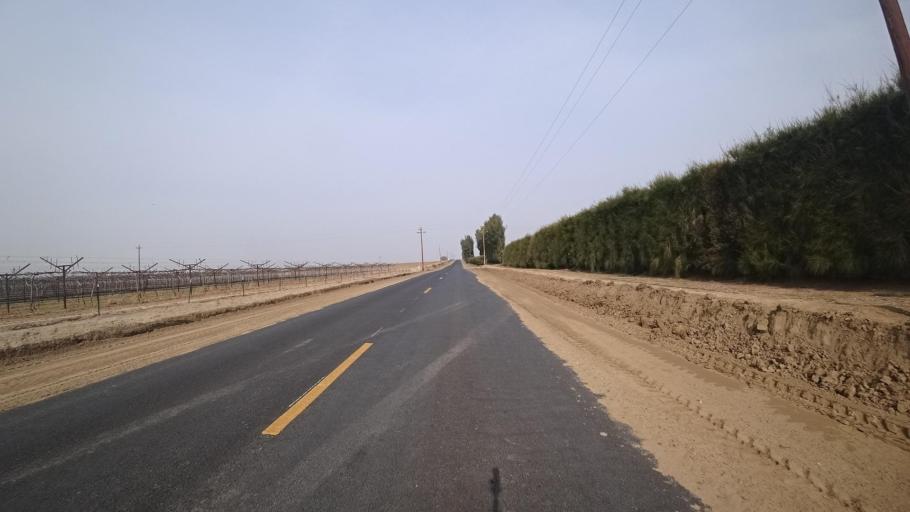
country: US
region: California
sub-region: Kern County
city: Arvin
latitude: 35.1063
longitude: -118.8505
